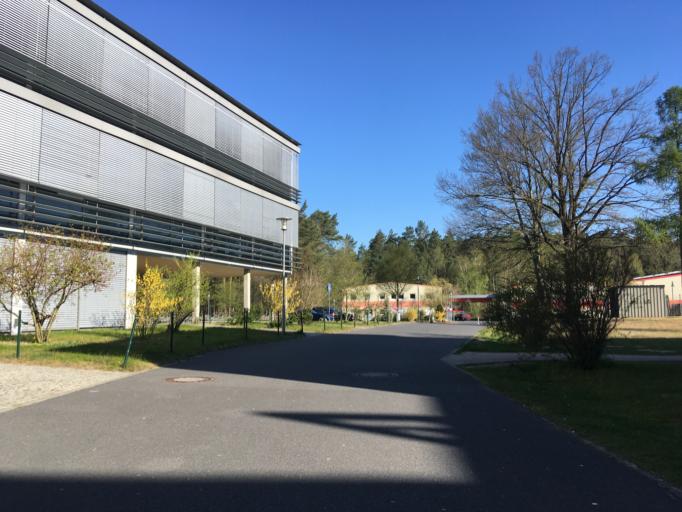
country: DE
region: Brandenburg
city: Bernau bei Berlin
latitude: 52.7073
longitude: 13.5428
